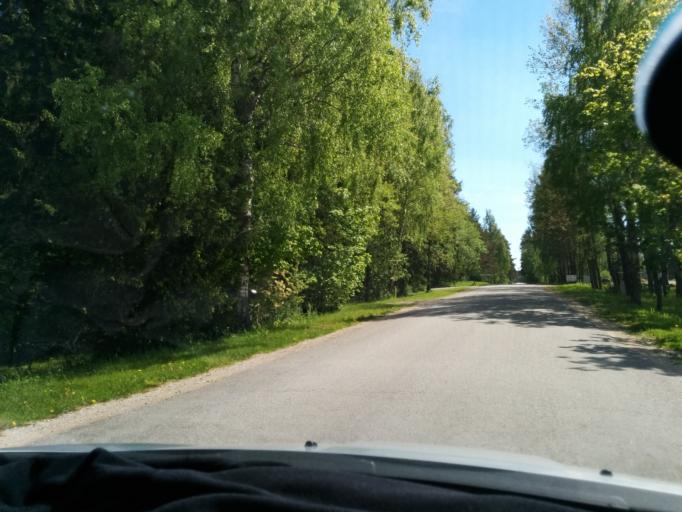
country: EE
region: Laeaene-Virumaa
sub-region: Tapa vald
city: Tapa
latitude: 59.5072
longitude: 25.9628
